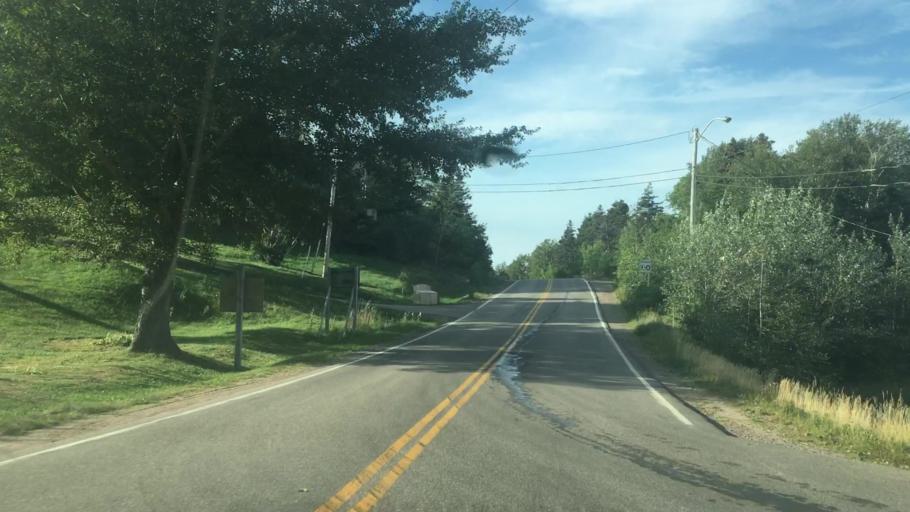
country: CA
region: Nova Scotia
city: Sydney Mines
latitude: 46.8231
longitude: -60.7998
